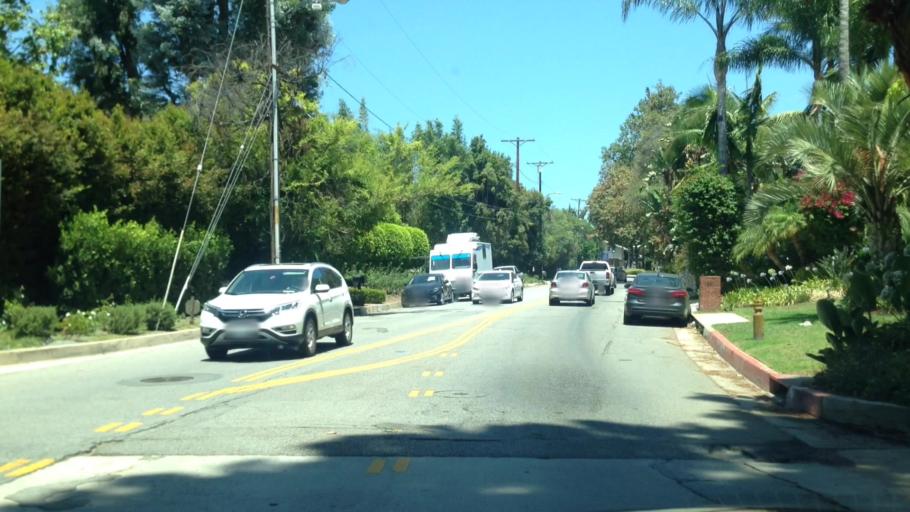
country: US
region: California
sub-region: Los Angeles County
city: Beverly Hills
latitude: 34.1014
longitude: -118.4062
